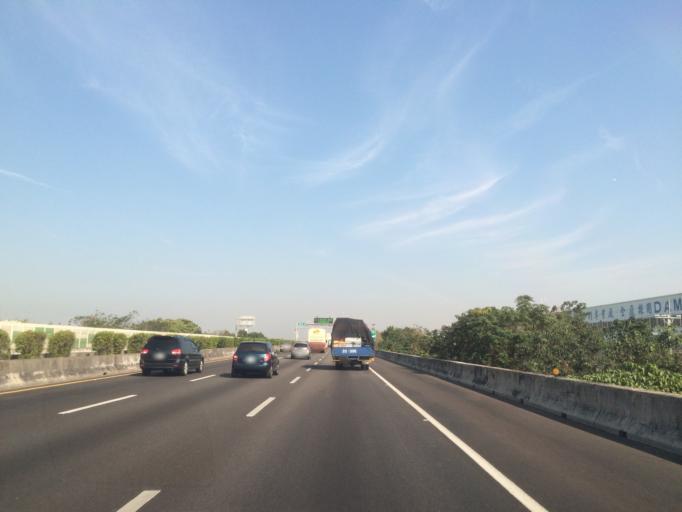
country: TW
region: Taiwan
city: Fengyuan
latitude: 24.2369
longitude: 120.6883
